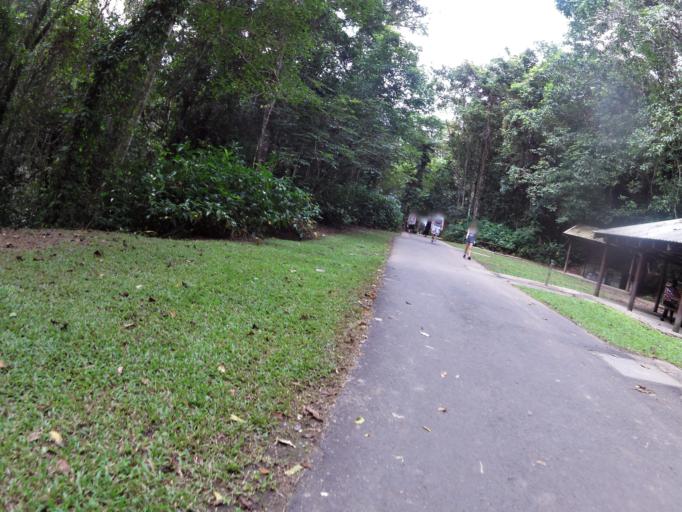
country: AU
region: Queensland
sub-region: Cairns
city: Woree
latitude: -16.9632
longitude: 145.6778
